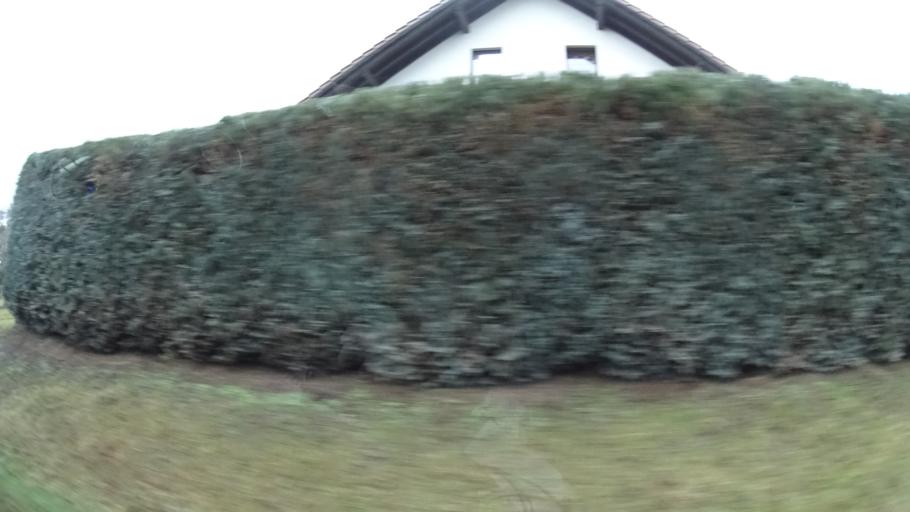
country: DE
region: Thuringia
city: Stepfershausen
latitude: 50.5972
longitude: 10.2981
